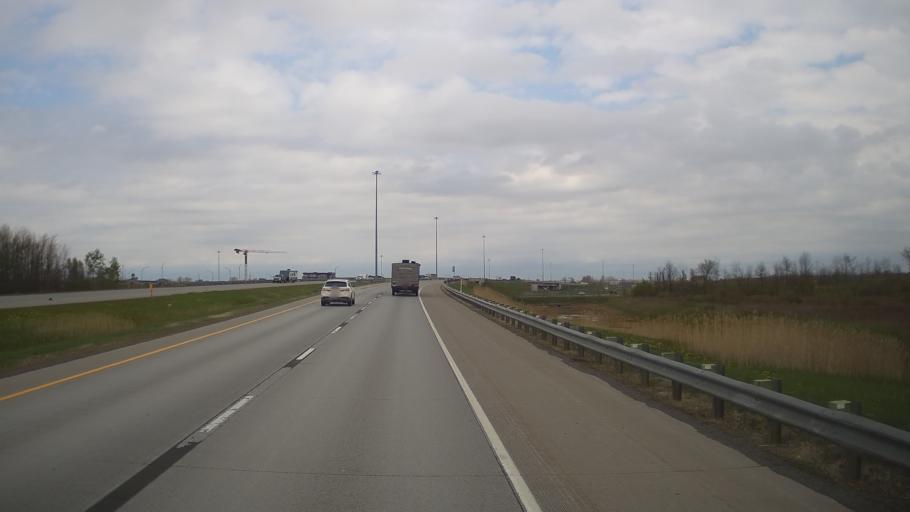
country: CA
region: Quebec
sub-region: Monteregie
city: Candiac
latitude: 45.3680
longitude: -73.5043
